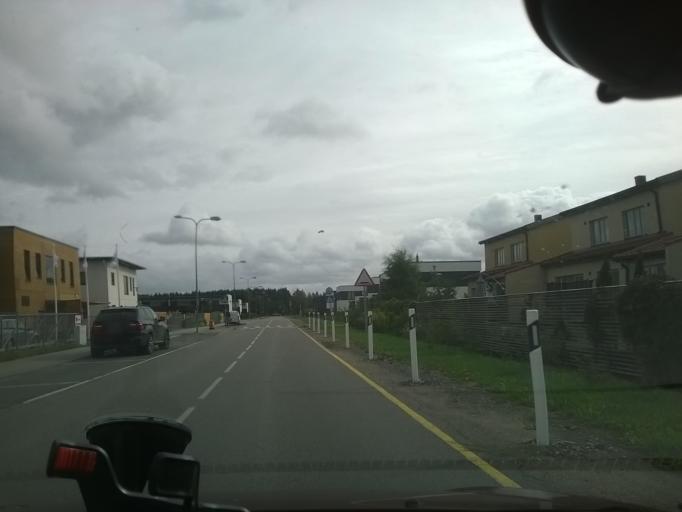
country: EE
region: Harju
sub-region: Tallinna linn
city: Tallinn
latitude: 59.4011
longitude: 24.8071
